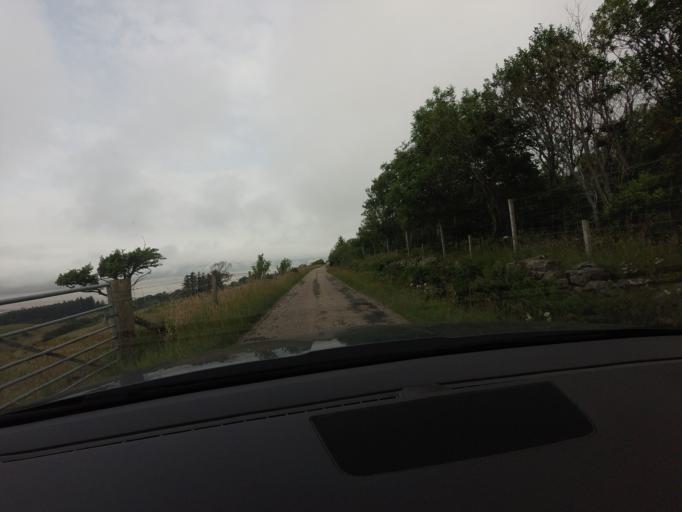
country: GB
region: Scotland
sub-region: Highland
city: Golspie
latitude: 58.4751
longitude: -4.4066
